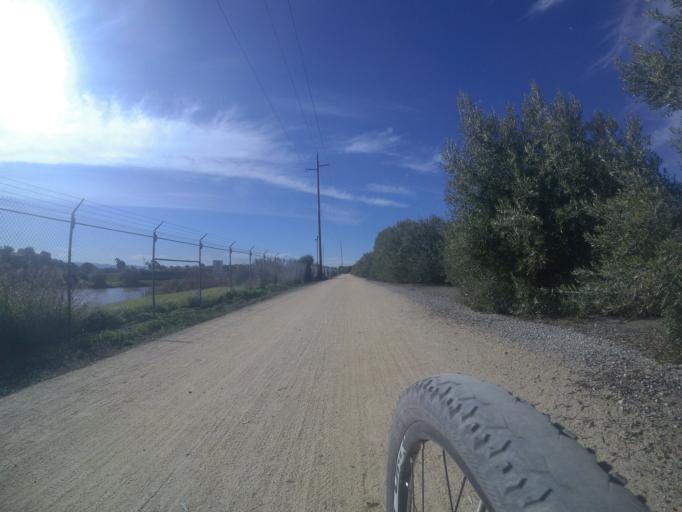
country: US
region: California
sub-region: Santa Clara County
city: Sunnyvale
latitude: 37.4259
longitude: -122.0321
